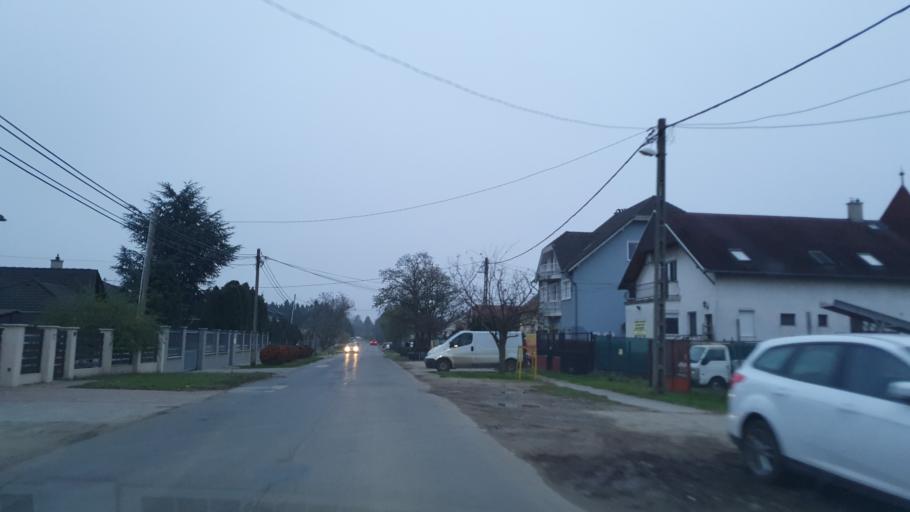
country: HU
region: Pest
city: Csomor
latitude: 47.5313
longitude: 19.2222
